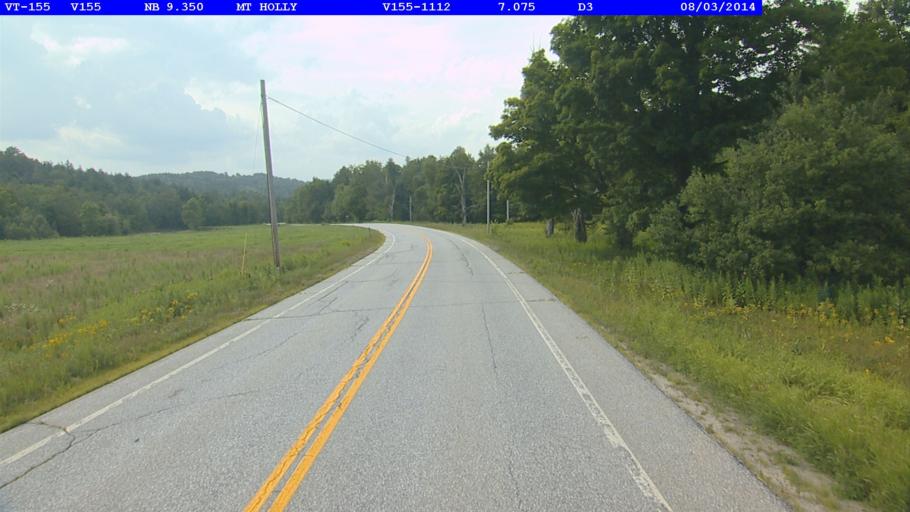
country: US
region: Vermont
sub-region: Rutland County
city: Rutland
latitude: 43.4422
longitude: -72.8666
